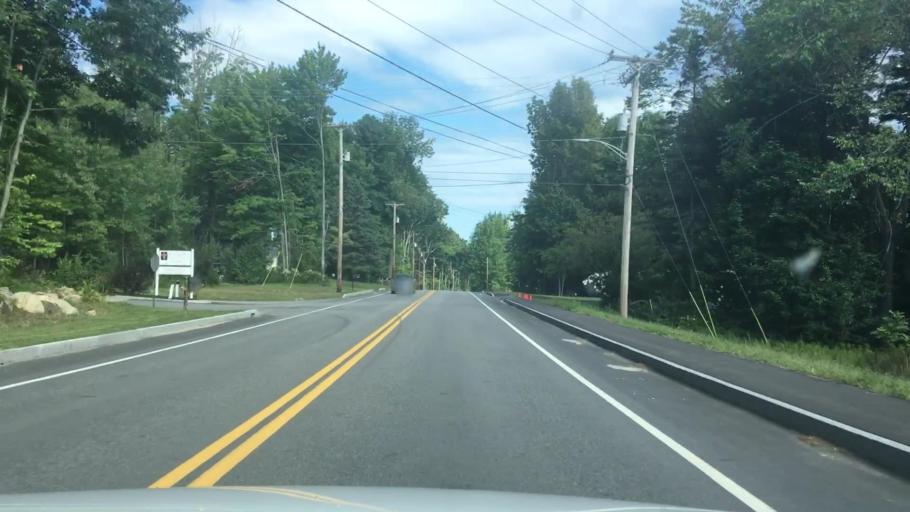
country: US
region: Maine
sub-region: Androscoggin County
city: Auburn
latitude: 44.1127
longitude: -70.2504
